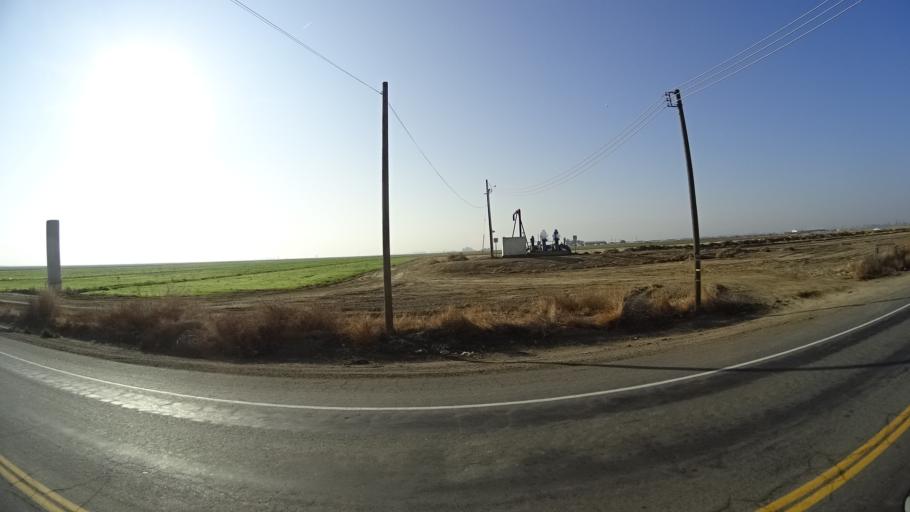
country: US
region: California
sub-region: Kern County
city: Greenfield
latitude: 35.2378
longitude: -118.9651
